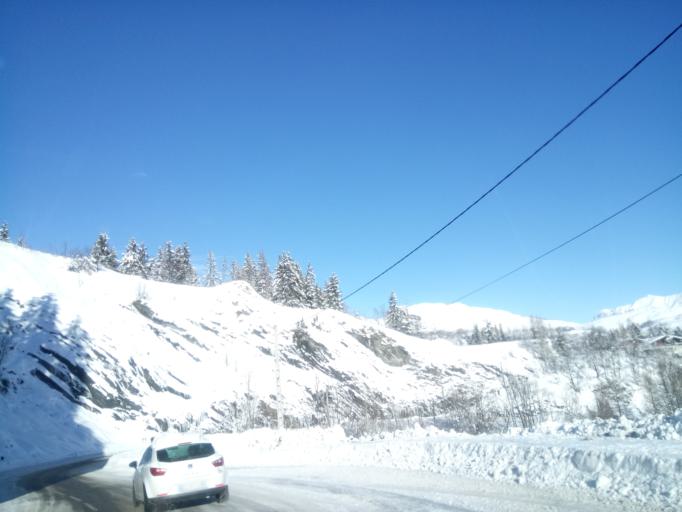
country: FR
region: Rhone-Alpes
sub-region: Departement de la Savoie
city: Saint-Jean-de-Maurienne
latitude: 45.2380
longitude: 6.2789
